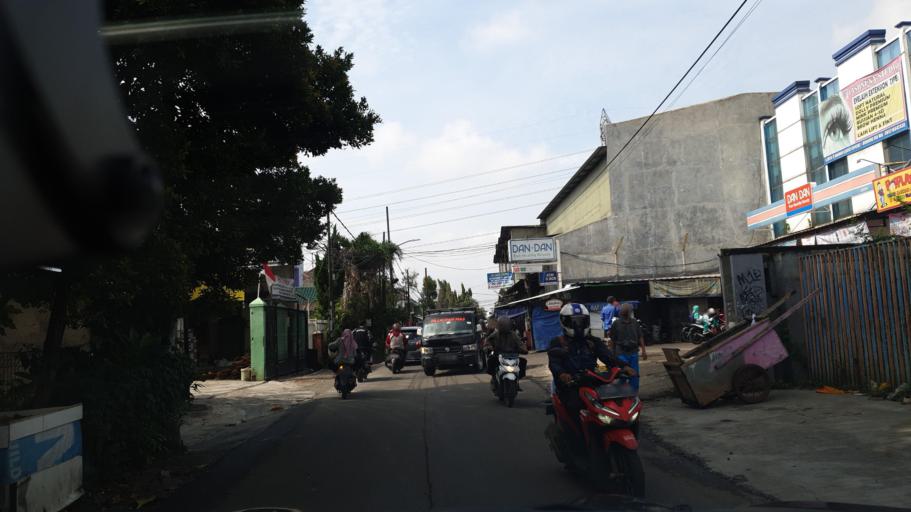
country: ID
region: West Java
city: Pamulang
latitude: -6.3140
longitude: 106.7544
